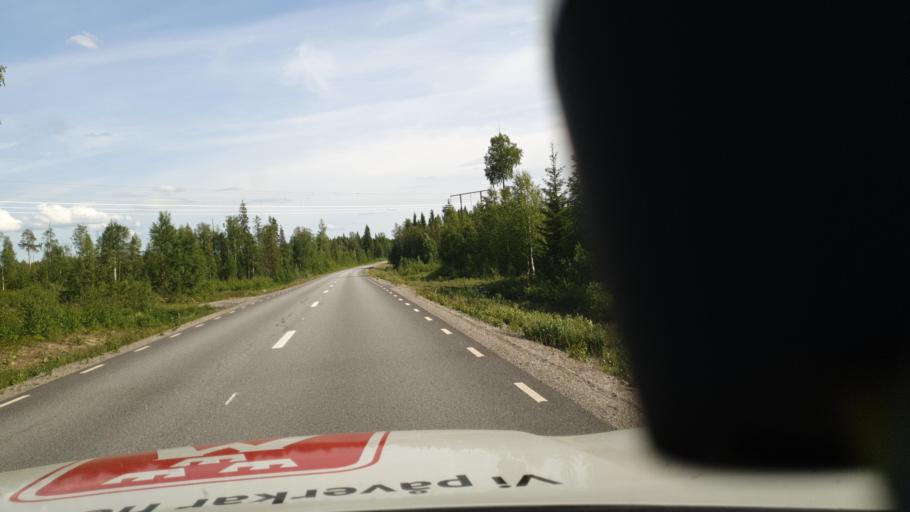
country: SE
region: Vaesterbotten
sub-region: Skelleftea Kommun
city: Forsbacka
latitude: 64.7248
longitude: 20.4104
